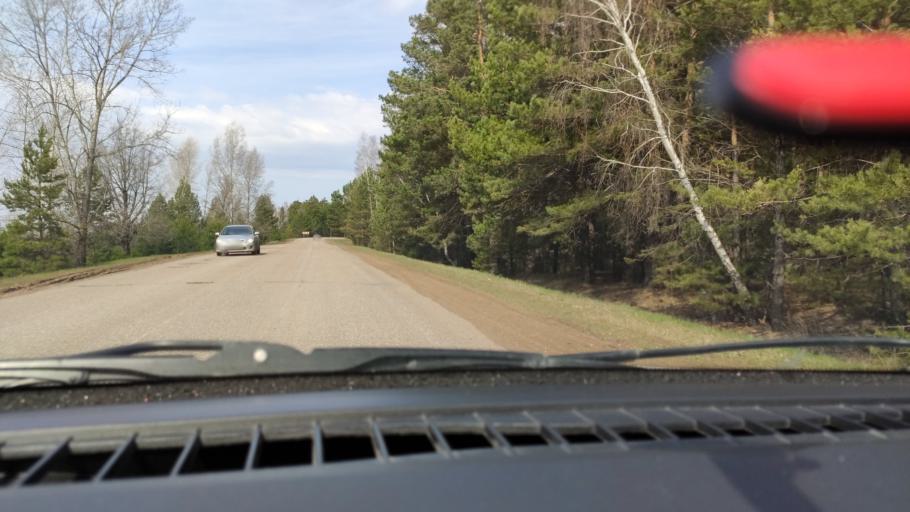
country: RU
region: Bashkortostan
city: Dyurtyuli
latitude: 55.5120
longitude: 54.8859
